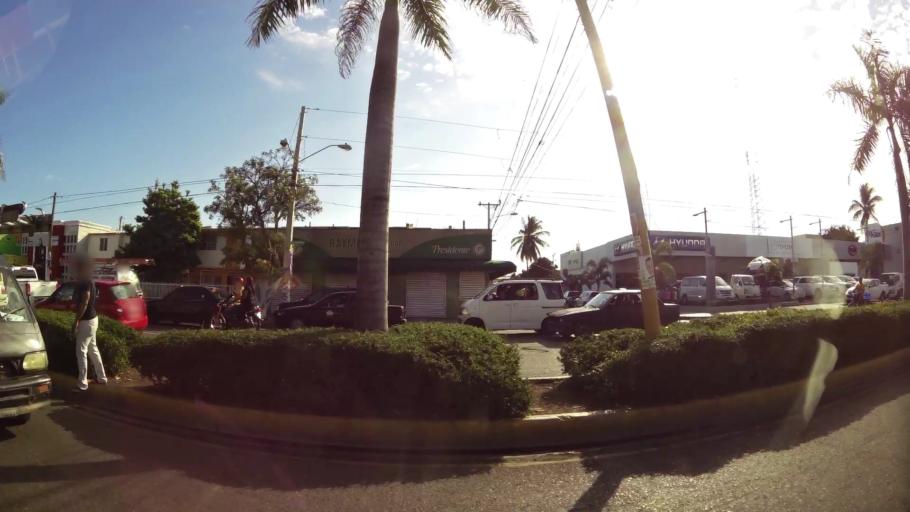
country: DO
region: Santo Domingo
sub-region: Santo Domingo
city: Santo Domingo Este
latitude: 18.4928
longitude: -69.8508
